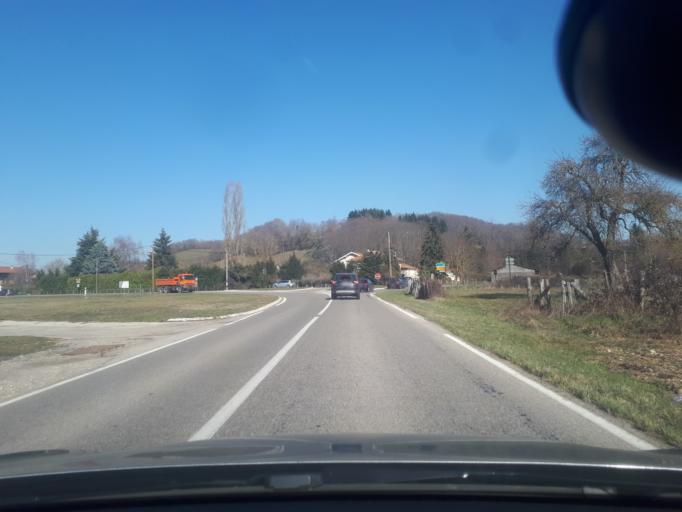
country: FR
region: Rhone-Alpes
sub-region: Departement de l'Isere
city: Champier
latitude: 45.4428
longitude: 5.2917
